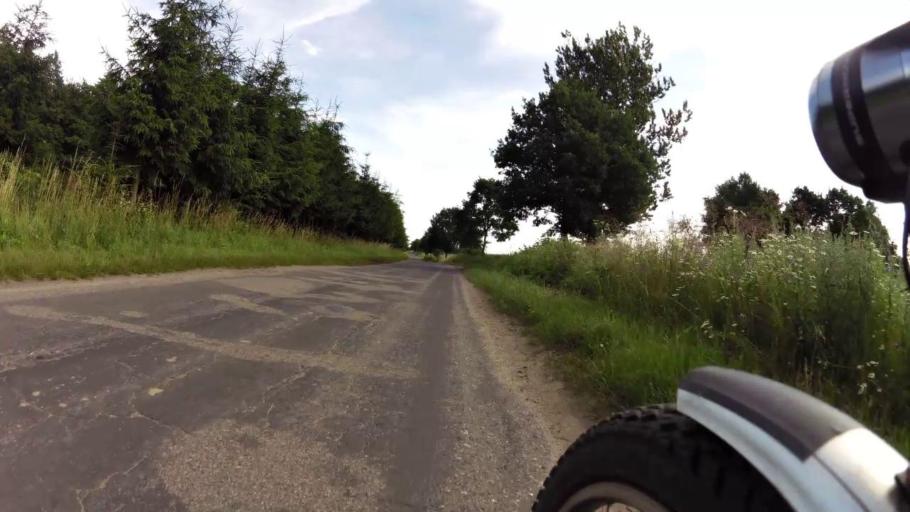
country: PL
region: West Pomeranian Voivodeship
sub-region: Powiat lobeski
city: Dobra
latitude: 53.5903
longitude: 15.3864
